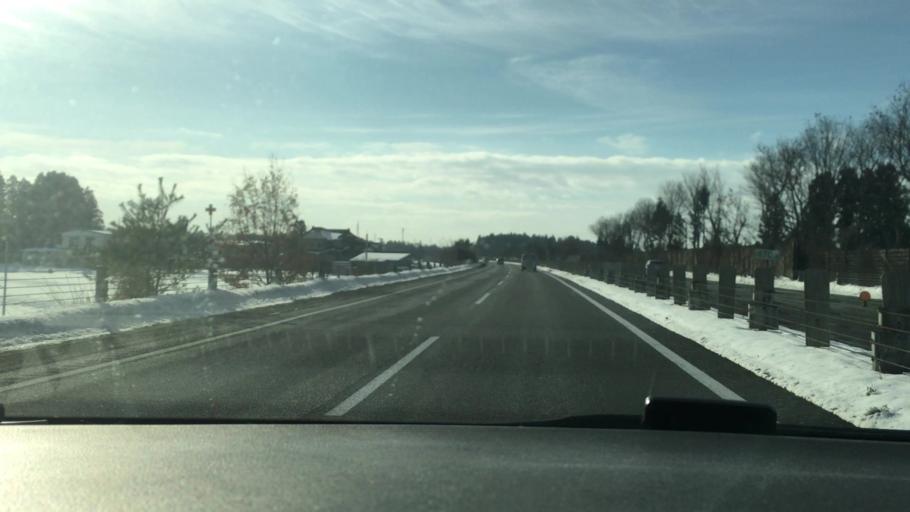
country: JP
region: Iwate
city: Hanamaki
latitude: 39.3550
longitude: 141.0893
